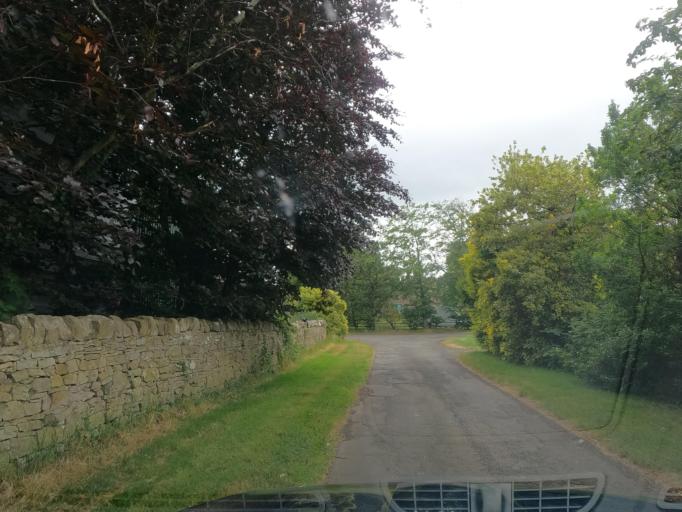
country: GB
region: England
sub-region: Northumberland
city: Lowick
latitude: 55.6512
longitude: -1.9085
